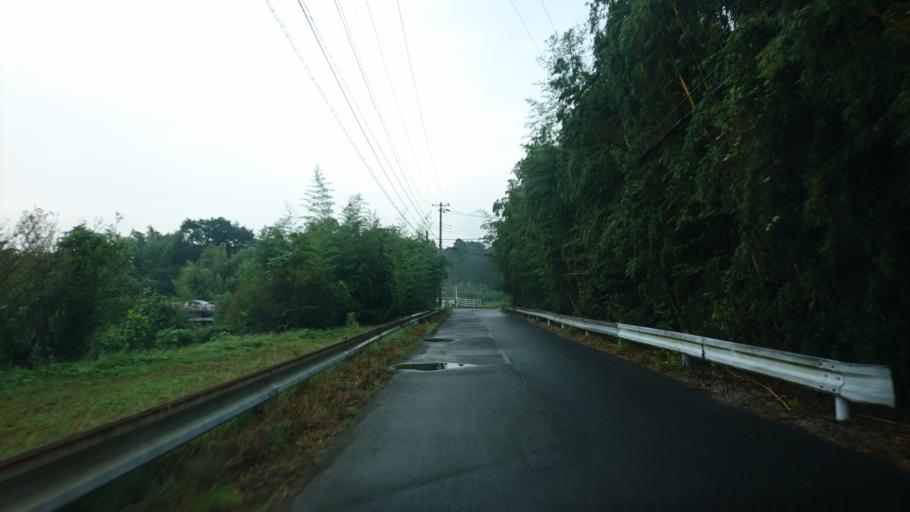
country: JP
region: Chiba
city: Kimitsu
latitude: 35.2991
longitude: 139.9826
